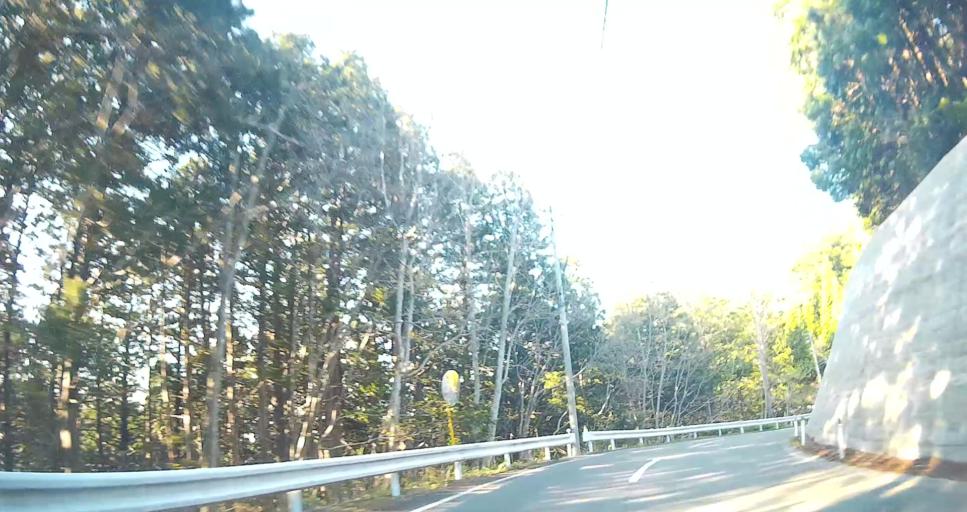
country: JP
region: Aomori
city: Mutsu
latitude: 41.3168
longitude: 141.1283
